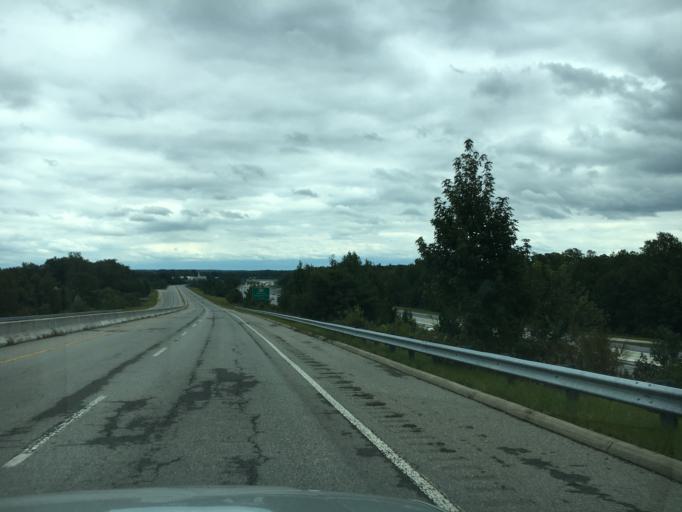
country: US
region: South Carolina
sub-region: Greenville County
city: Mauldin
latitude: 34.7576
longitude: -82.2858
